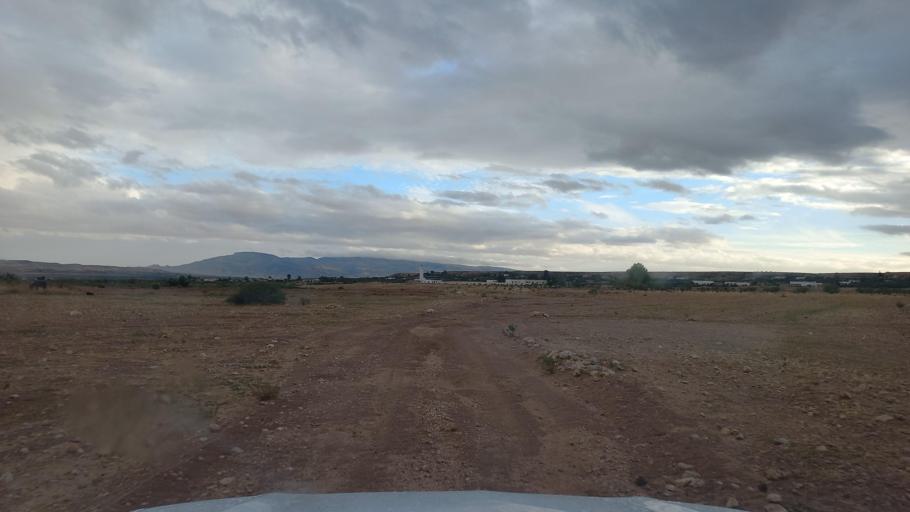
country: TN
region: Al Qasrayn
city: Kasserine
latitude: 35.2707
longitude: 8.9363
